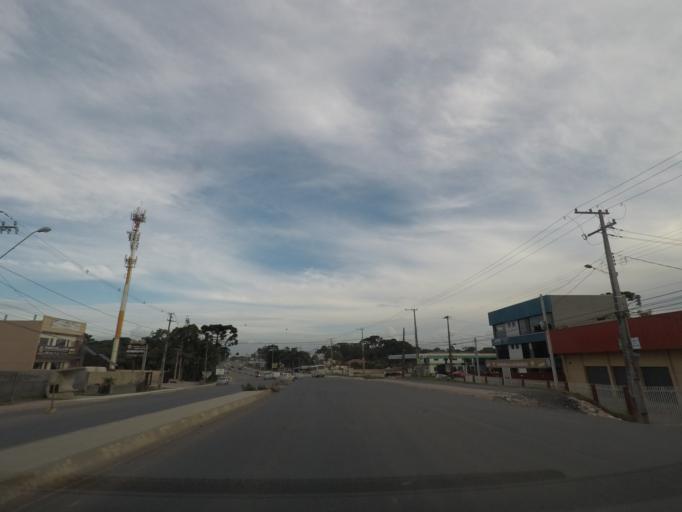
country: BR
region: Parana
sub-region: Colombo
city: Colombo
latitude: -25.3154
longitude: -49.2209
